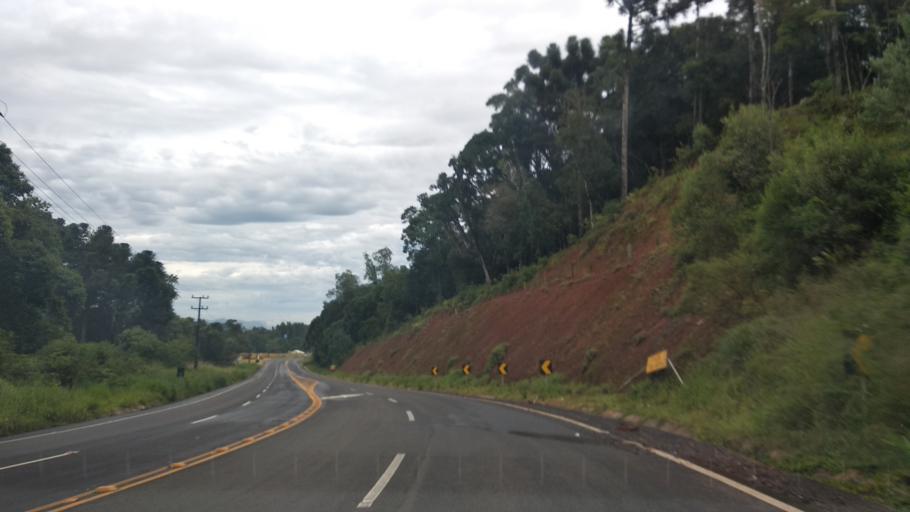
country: BR
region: Santa Catarina
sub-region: Videira
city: Videira
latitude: -27.0518
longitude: -51.1836
